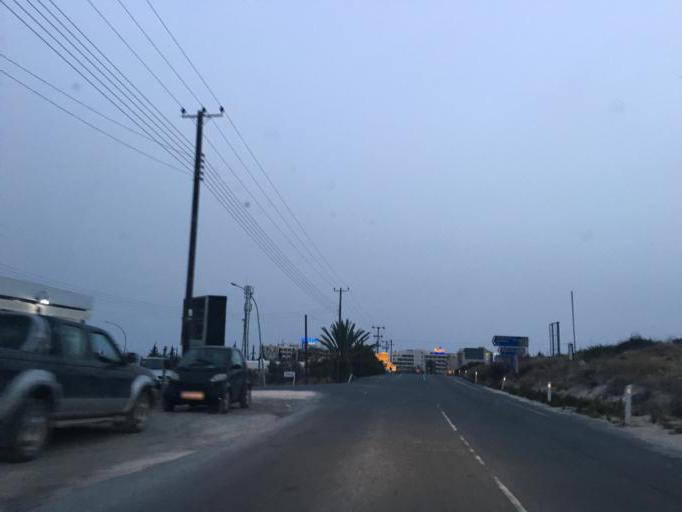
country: CY
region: Larnaka
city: Agios Tychon
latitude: 34.7178
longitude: 33.1632
